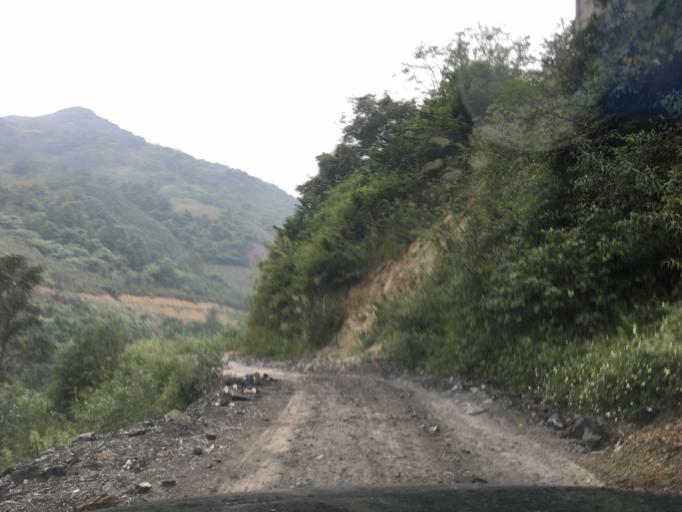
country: CN
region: Guangxi Zhuangzu Zizhiqu
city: Xinzhou
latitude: 25.0499
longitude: 105.9203
